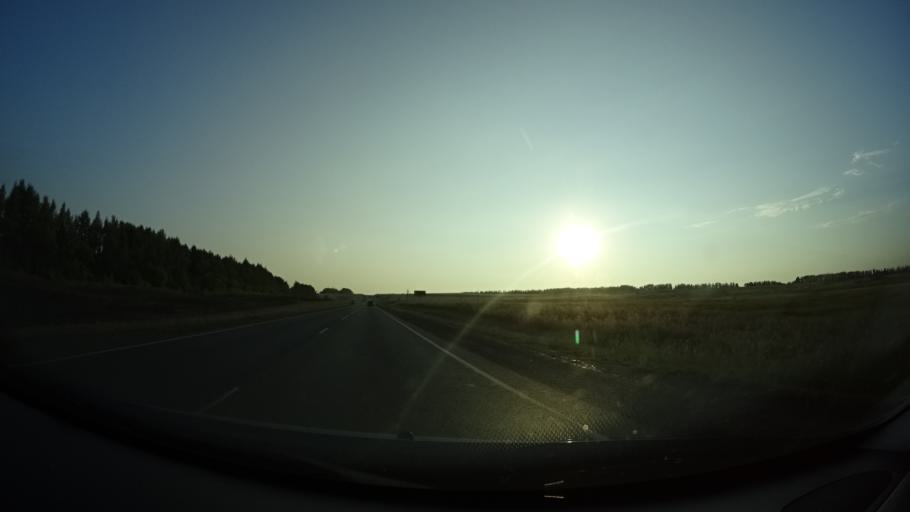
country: RU
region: Samara
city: Klyavlino
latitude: 54.0218
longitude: 51.8330
